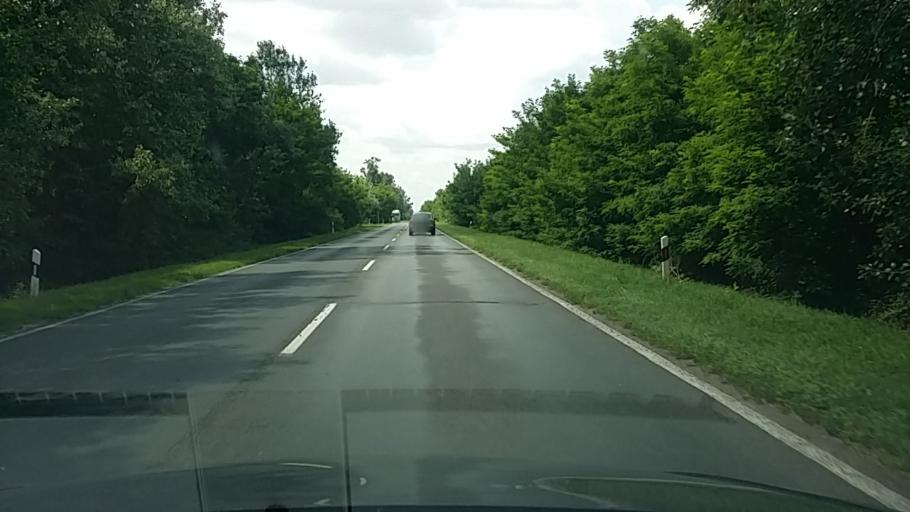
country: HU
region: Bacs-Kiskun
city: Lajosmizse
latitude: 46.9955
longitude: 19.6023
